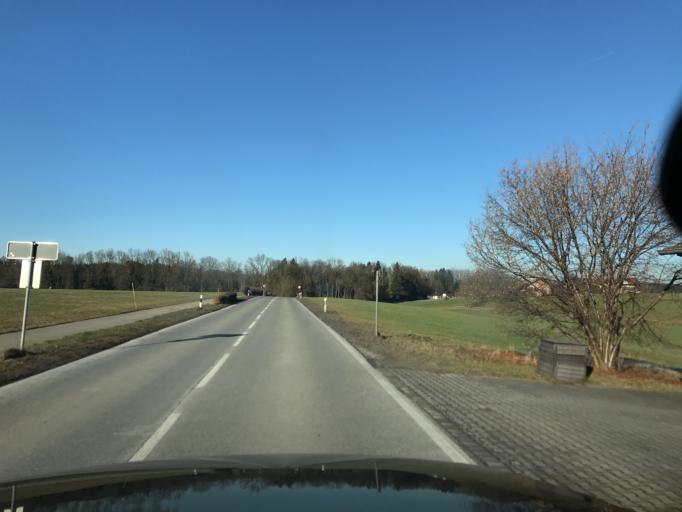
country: DE
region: Bavaria
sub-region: Upper Bavaria
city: Rosenheim
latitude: 47.8683
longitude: 12.1521
